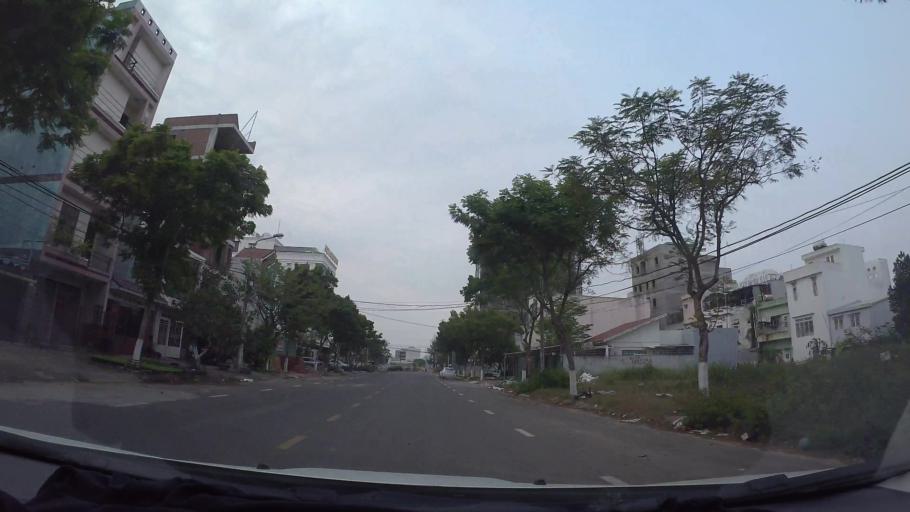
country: VN
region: Da Nang
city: Son Tra
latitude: 16.0479
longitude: 108.2436
